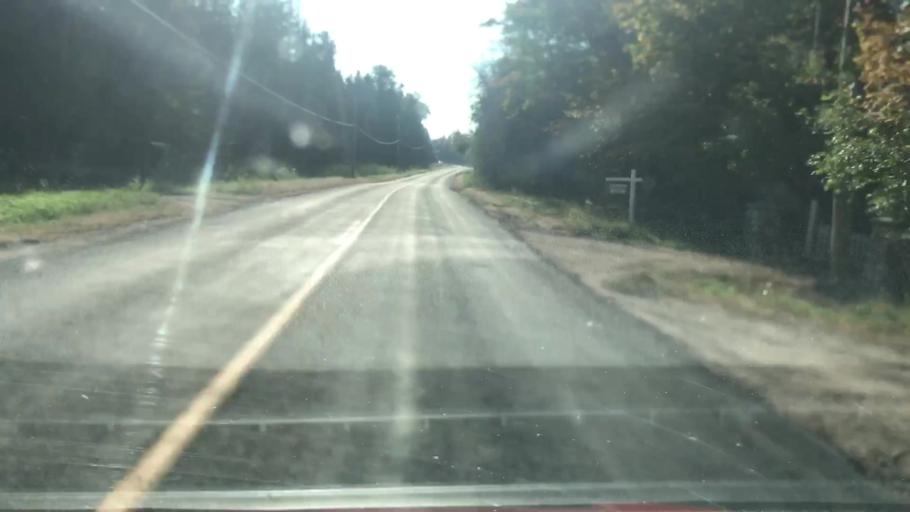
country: US
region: Michigan
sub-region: Chippewa County
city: Sault Ste. Marie
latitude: 46.2883
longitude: -84.0465
